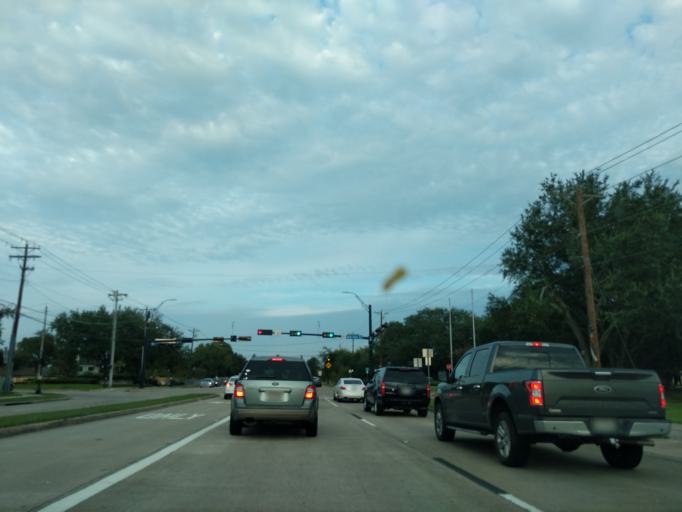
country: US
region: Texas
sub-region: Galveston County
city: Clear Lake Shores
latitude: 29.5262
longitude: -95.0489
